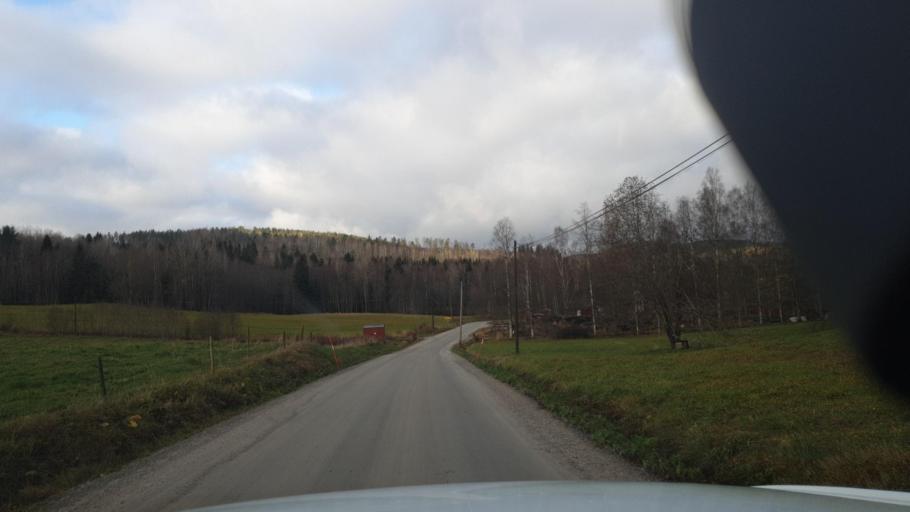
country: SE
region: Vaermland
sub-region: Sunne Kommun
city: Sunne
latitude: 59.6895
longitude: 12.8901
